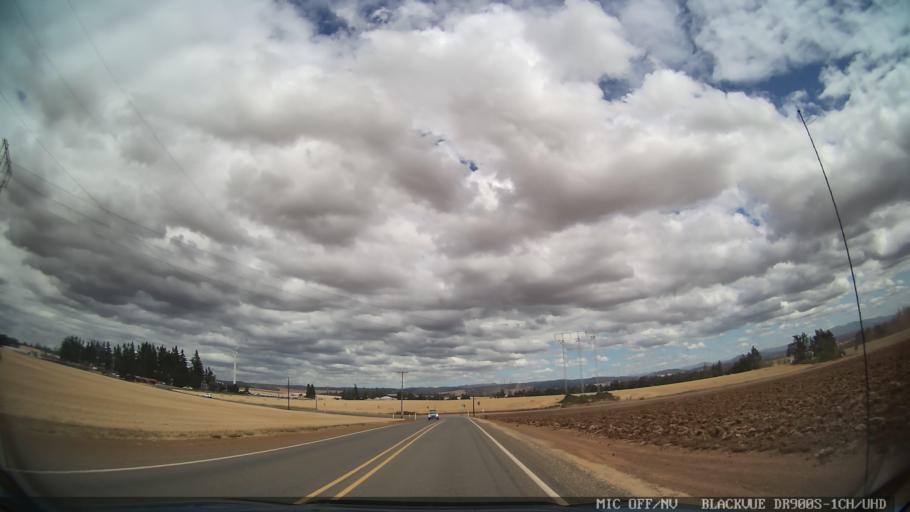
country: US
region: Oregon
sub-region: Marion County
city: Sublimity
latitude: 44.8653
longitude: -122.8126
